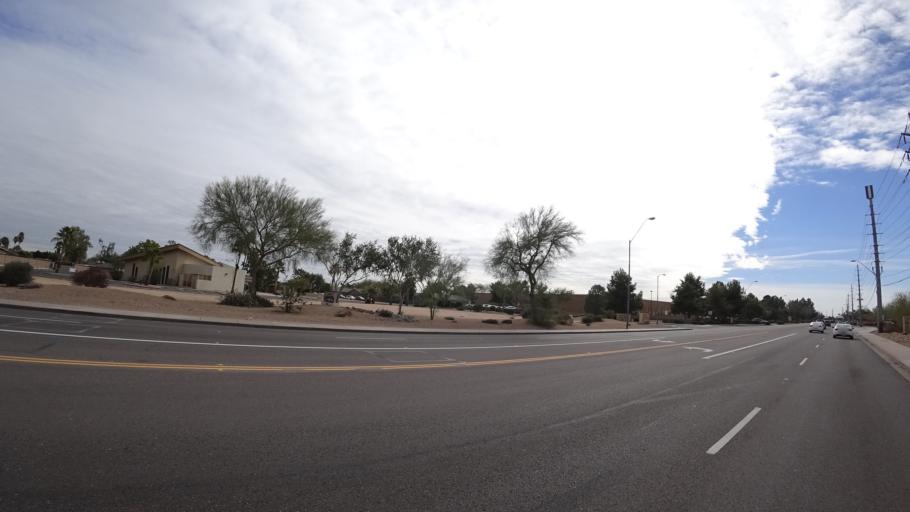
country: US
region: Arizona
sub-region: Maricopa County
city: Peoria
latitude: 33.6435
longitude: -112.1865
